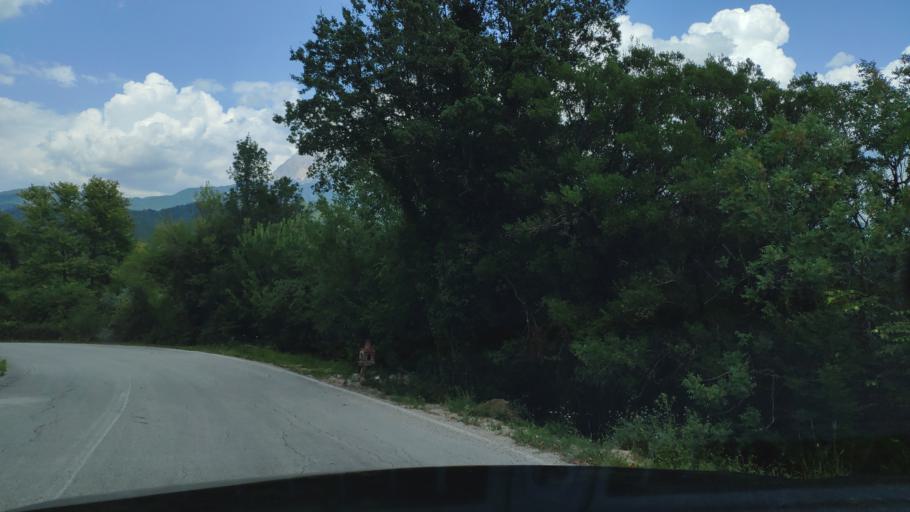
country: GR
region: Epirus
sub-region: Nomos Artas
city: Agios Dimitrios
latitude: 39.4512
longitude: 21.0290
